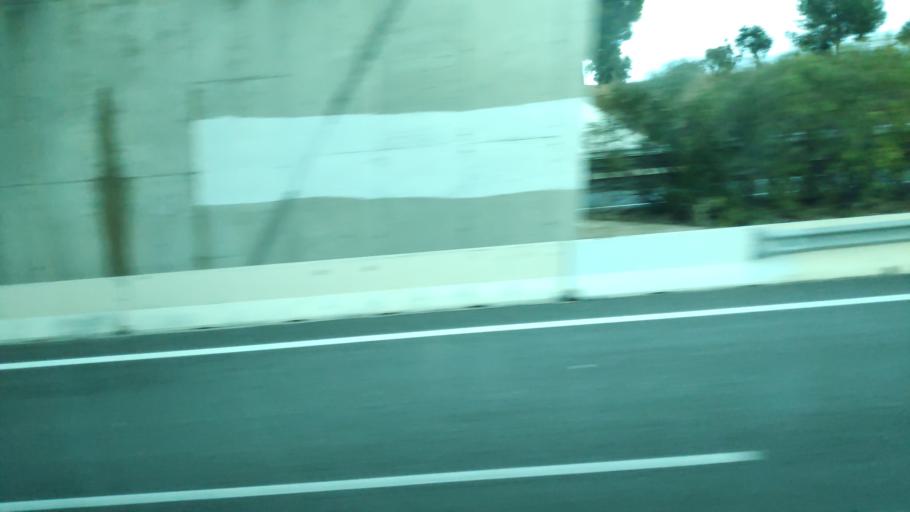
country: ES
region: Castille-La Mancha
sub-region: Provincia de Cuenca
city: Tarancon
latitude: 40.0103
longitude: -3.0296
